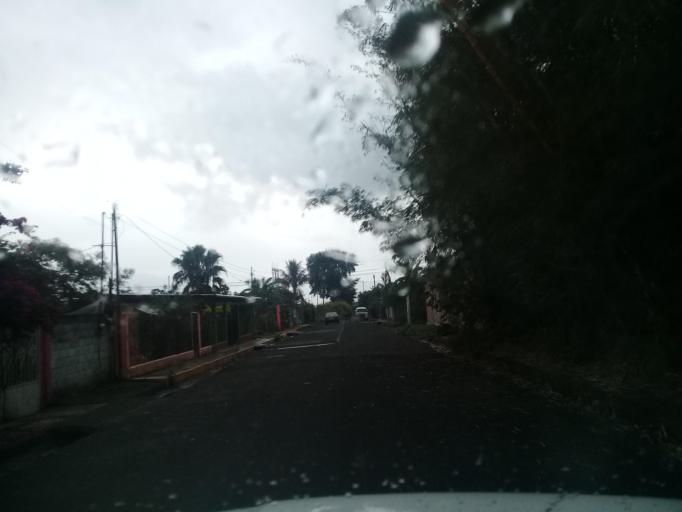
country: MX
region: Veracruz
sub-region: Cordoba
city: Veinte de Noviembre
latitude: 18.8625
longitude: -96.9550
